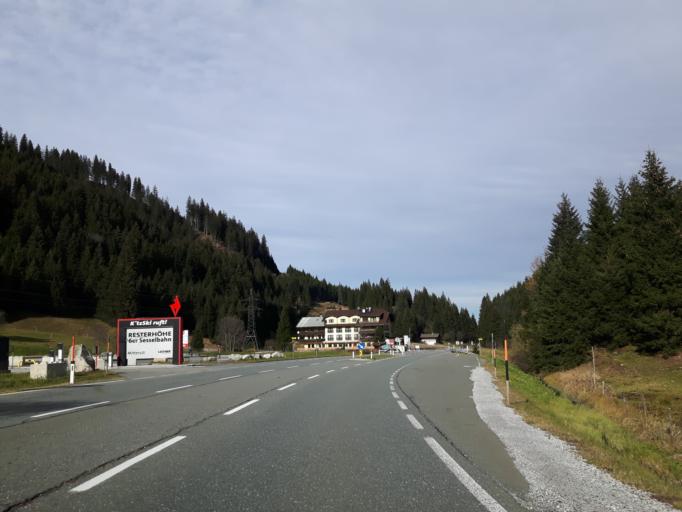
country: AT
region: Salzburg
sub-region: Politischer Bezirk Zell am See
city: Hollersbach im Pinzgau
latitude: 47.3226
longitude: 12.4097
